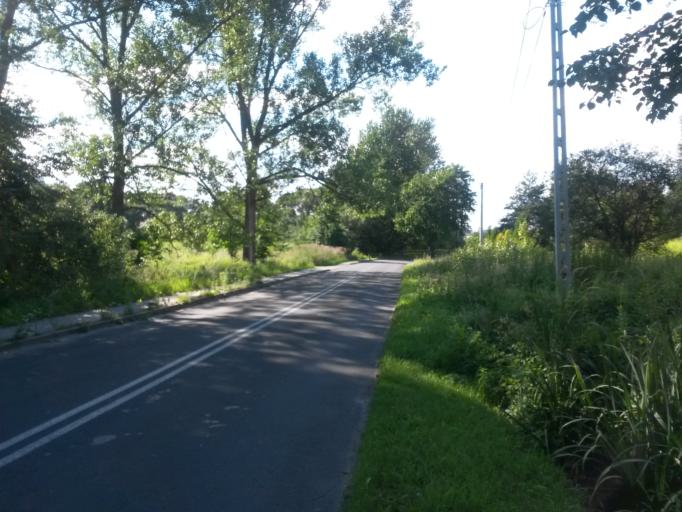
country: PL
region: Silesian Voivodeship
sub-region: Powiat bedzinski
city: Siewierz
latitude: 50.4635
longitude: 19.2424
